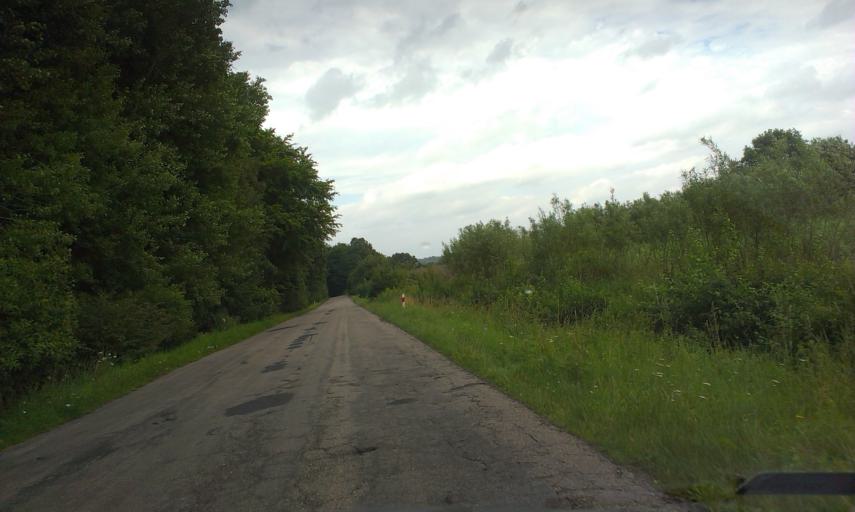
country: PL
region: West Pomeranian Voivodeship
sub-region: Powiat szczecinecki
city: Barwice
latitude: 53.6914
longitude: 16.3450
